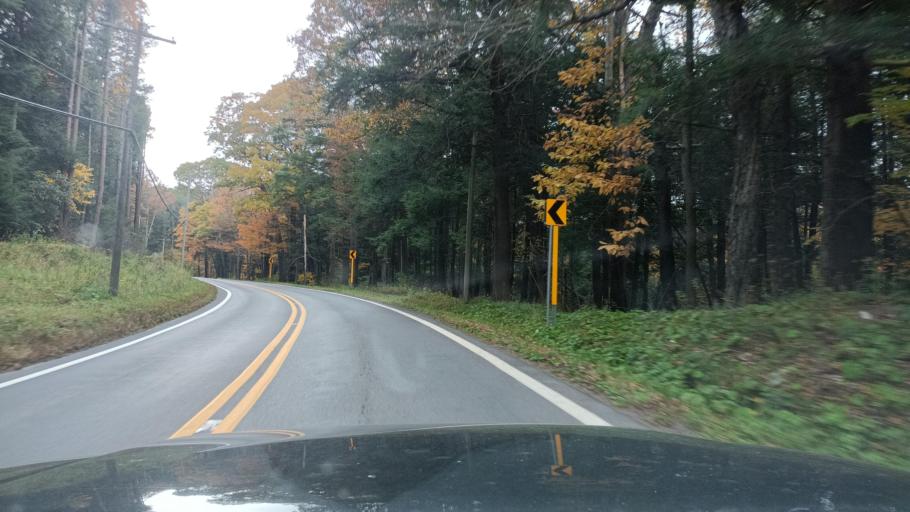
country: US
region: West Virginia
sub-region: Preston County
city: Terra Alta
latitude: 39.3256
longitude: -79.5380
